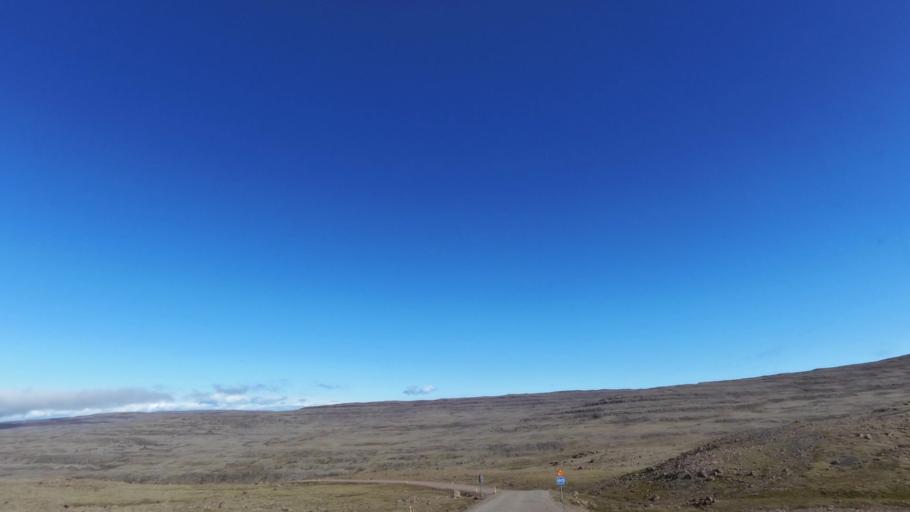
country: IS
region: West
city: Olafsvik
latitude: 65.5521
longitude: -24.2190
